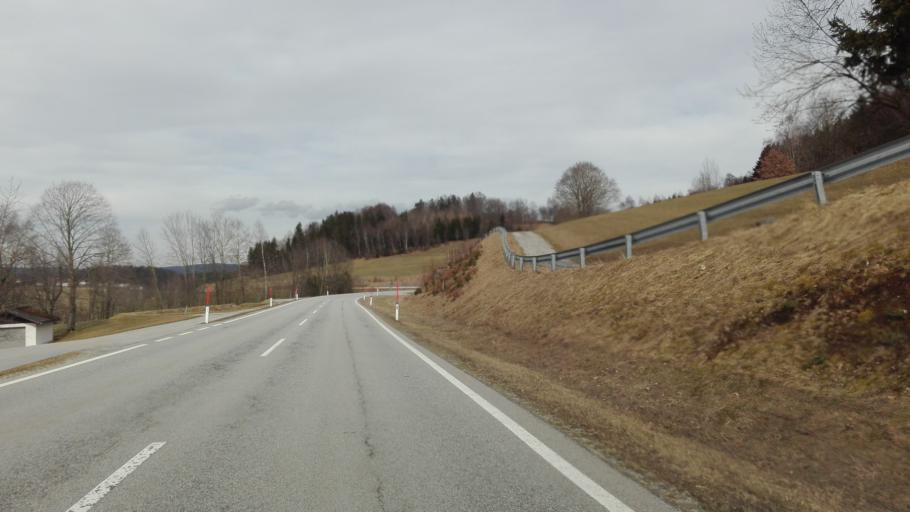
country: AT
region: Upper Austria
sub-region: Politischer Bezirk Rohrbach
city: Nebelberg
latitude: 48.6125
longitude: 13.8488
